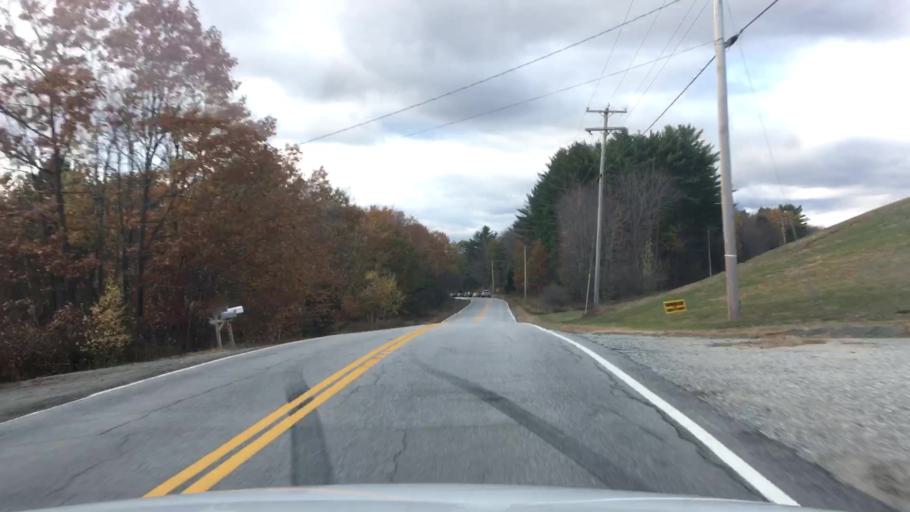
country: US
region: Maine
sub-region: Androscoggin County
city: Leeds
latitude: 44.3286
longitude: -70.1228
